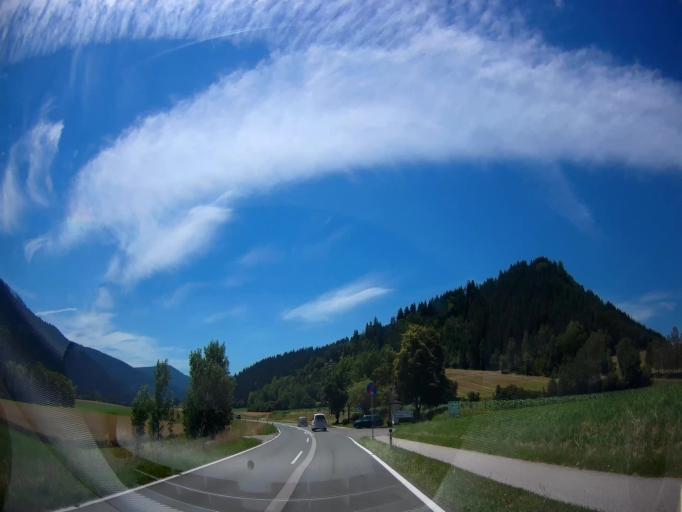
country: AT
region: Carinthia
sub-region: Politischer Bezirk Sankt Veit an der Glan
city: Strassburg
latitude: 46.8922
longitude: 14.3215
